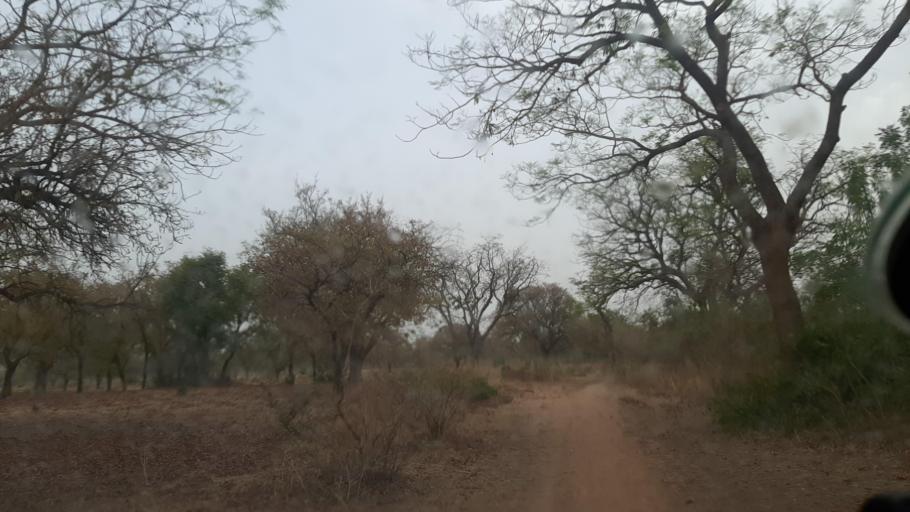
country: BF
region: Boucle du Mouhoun
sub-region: Province des Banwa
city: Salanso
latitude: 11.8595
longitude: -4.4343
